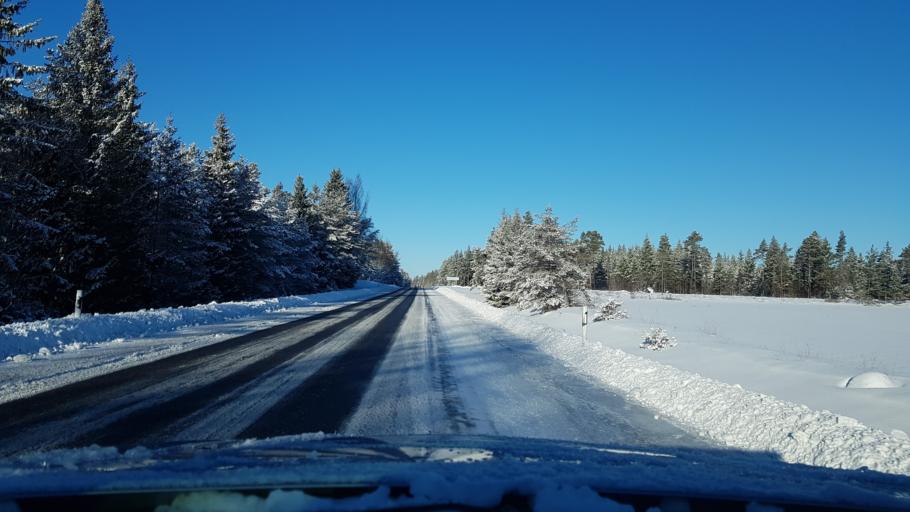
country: EE
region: Hiiumaa
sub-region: Kaerdla linn
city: Kardla
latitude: 58.9697
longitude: 22.8280
